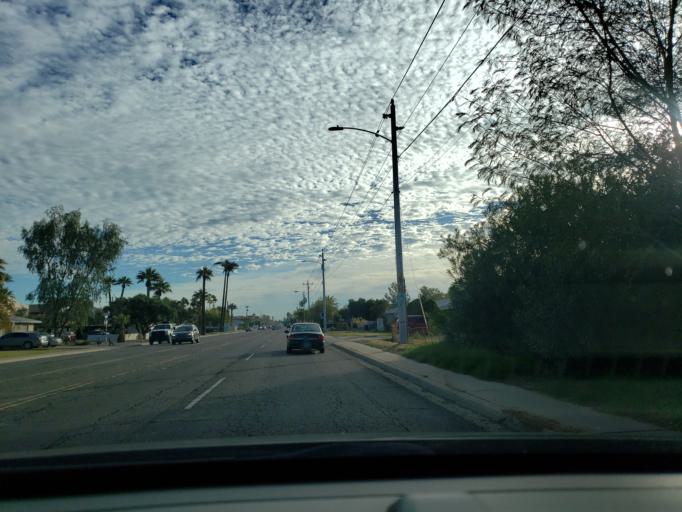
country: US
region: Arizona
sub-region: Maricopa County
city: Phoenix
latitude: 33.4871
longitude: -112.0547
